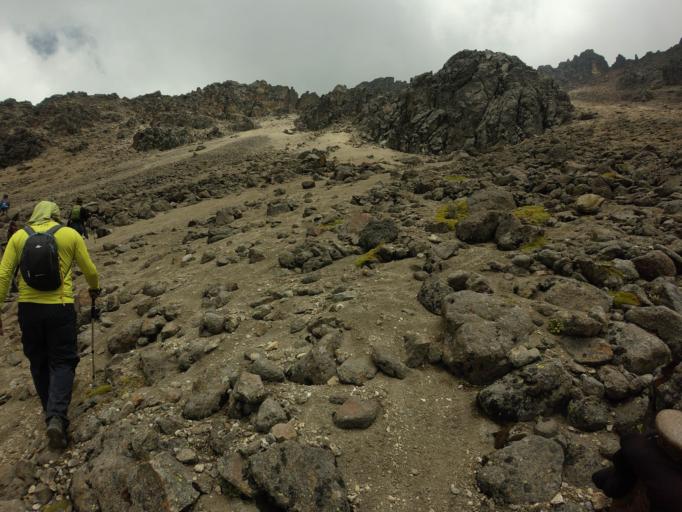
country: MX
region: Mexico
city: Amecameca de Juarez
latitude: 19.1513
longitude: -98.6391
